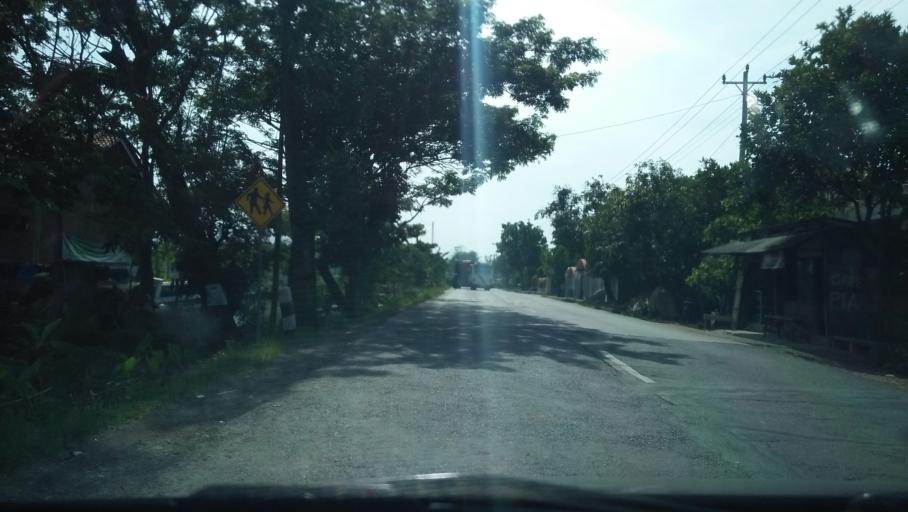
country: ID
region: Central Java
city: Welahan
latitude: -6.8542
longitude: 110.7071
